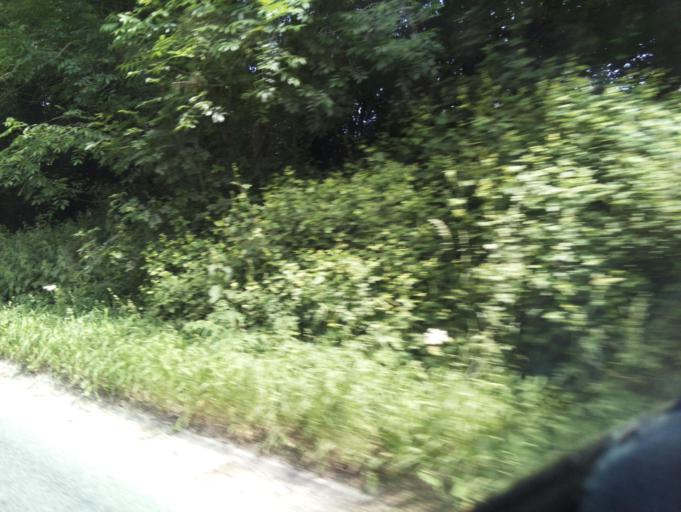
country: GB
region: England
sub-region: Somerset
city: Wincanton
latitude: 51.0525
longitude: -2.4409
